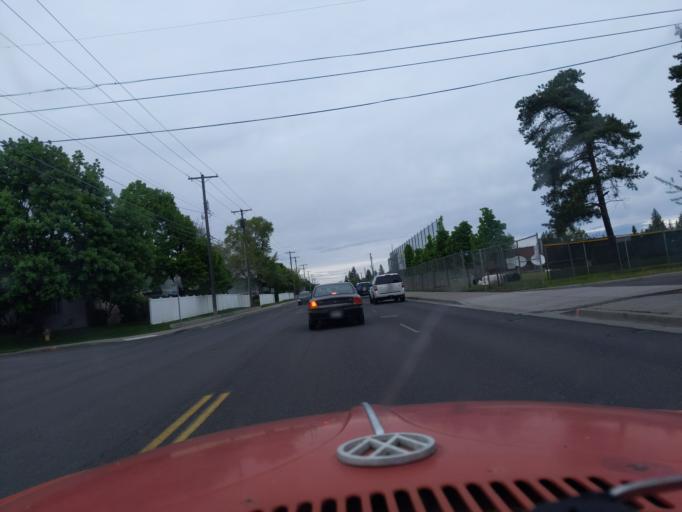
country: US
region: Washington
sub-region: Spokane County
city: Spokane
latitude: 47.6171
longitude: -117.3686
